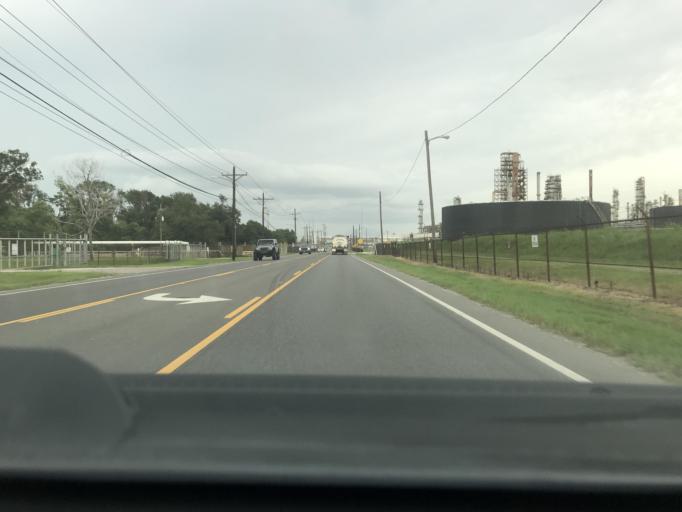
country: US
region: Louisiana
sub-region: Calcasieu Parish
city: Westlake
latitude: 30.2456
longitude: -93.2801
